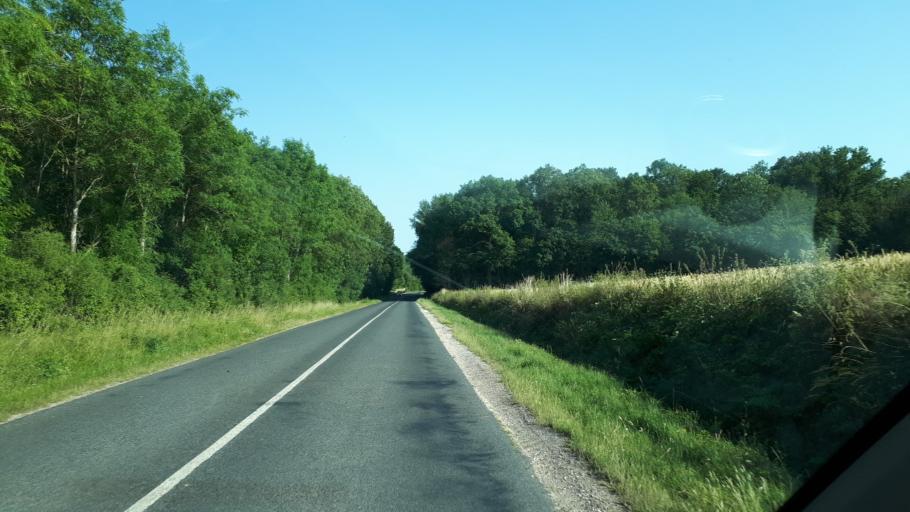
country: FR
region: Centre
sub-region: Departement du Loir-et-Cher
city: La Ville-aux-Clercs
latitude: 47.9340
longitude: 1.0829
